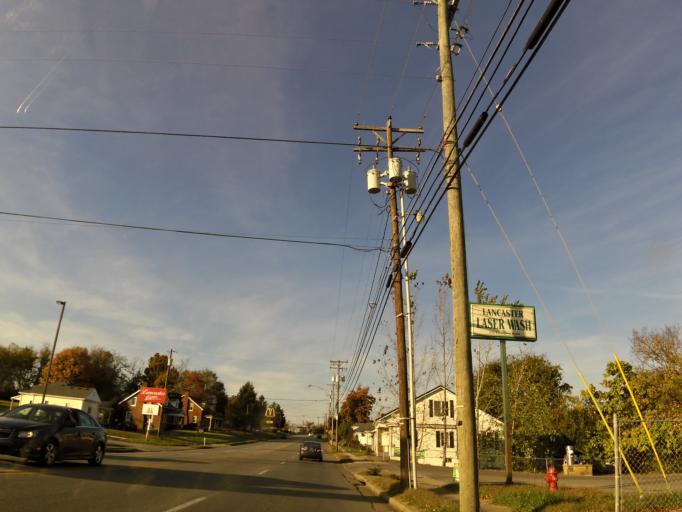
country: US
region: Kentucky
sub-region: Garrard County
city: Lancaster
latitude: 37.6254
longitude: -84.5792
